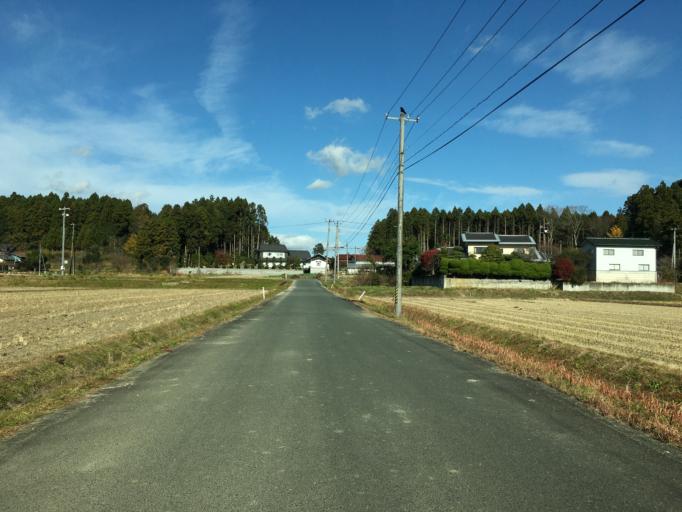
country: JP
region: Miyagi
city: Marumori
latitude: 37.8931
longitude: 140.9115
